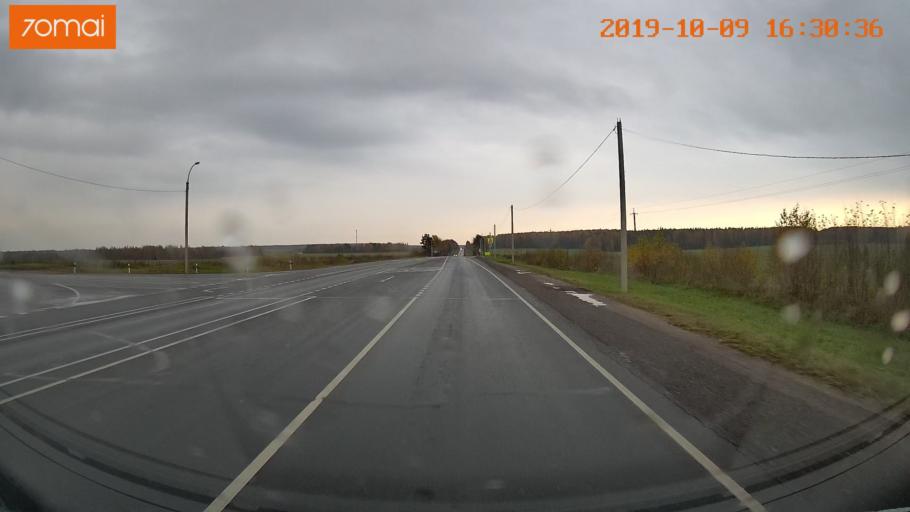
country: RU
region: Kostroma
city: Oktyabr'skiy
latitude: 57.6172
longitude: 40.9420
